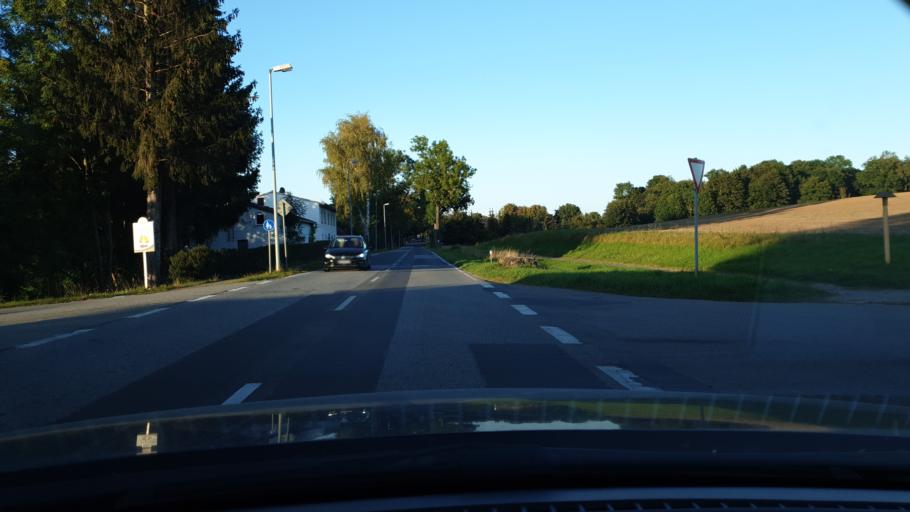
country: DE
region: Mecklenburg-Vorpommern
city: Lutzow
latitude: 53.6225
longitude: 11.1531
